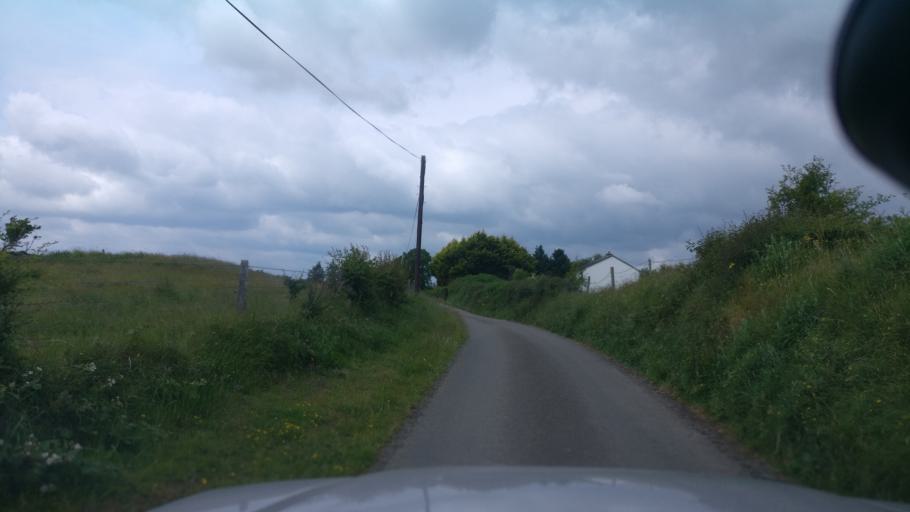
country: IE
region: Connaught
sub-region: County Galway
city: Ballinasloe
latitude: 53.2898
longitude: -8.3173
